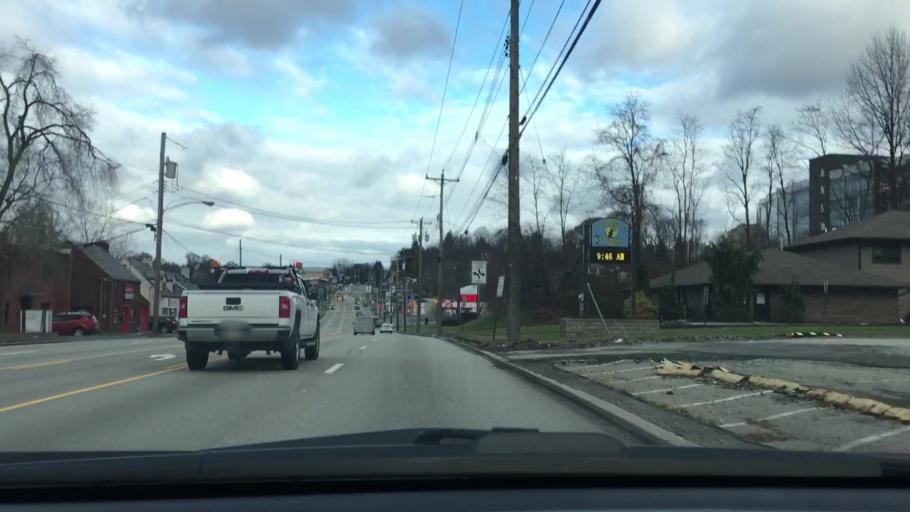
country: US
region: Pennsylvania
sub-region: Allegheny County
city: Whitehall
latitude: 40.3542
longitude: -79.9787
